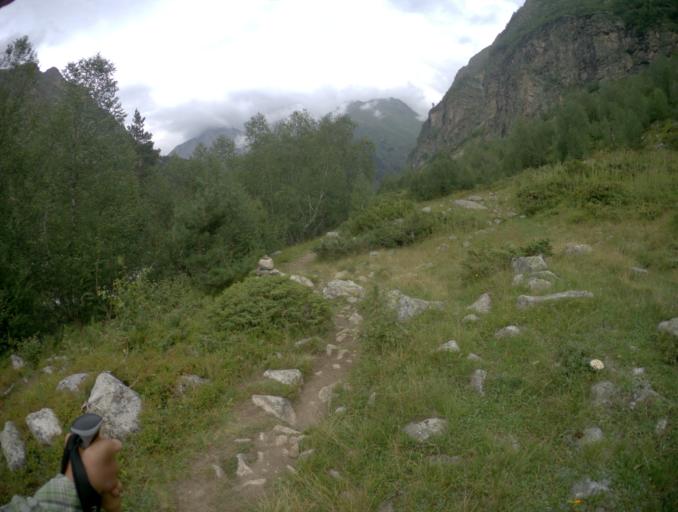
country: RU
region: Karachayevo-Cherkesiya
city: Uchkulan
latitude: 43.2693
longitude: 42.1514
